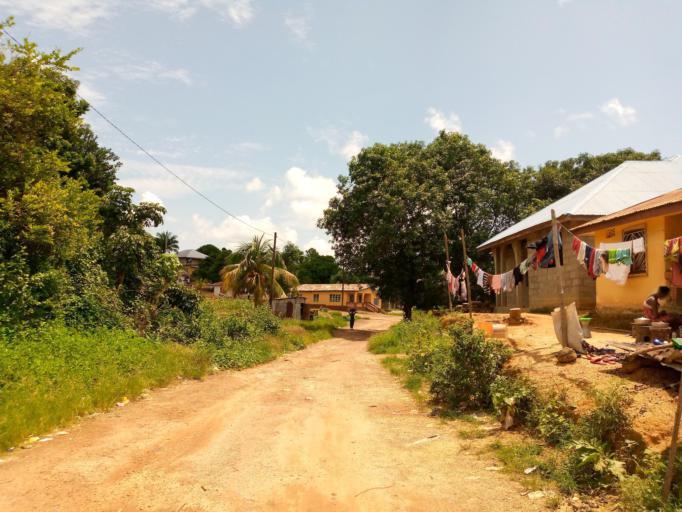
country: SL
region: Northern Province
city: Magburaka
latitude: 8.7264
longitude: -11.9418
